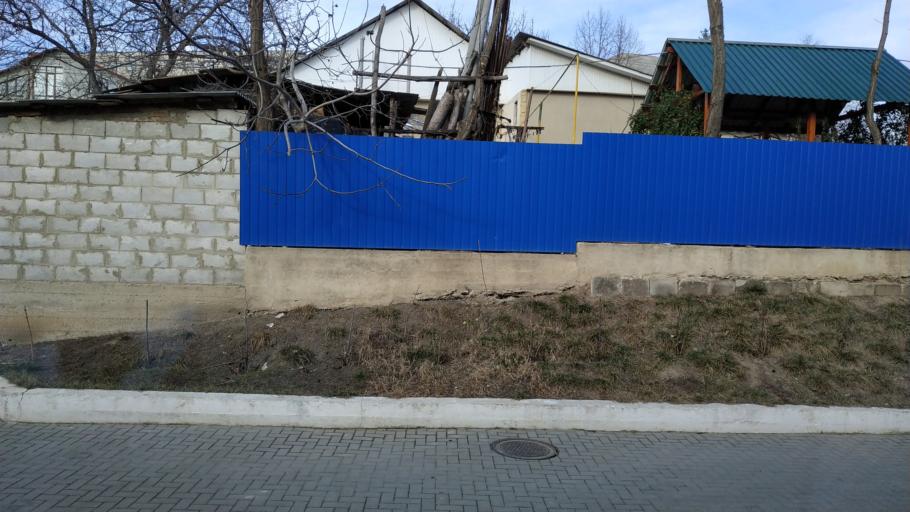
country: MD
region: Nisporeni
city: Nisporeni
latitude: 47.0826
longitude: 28.1876
